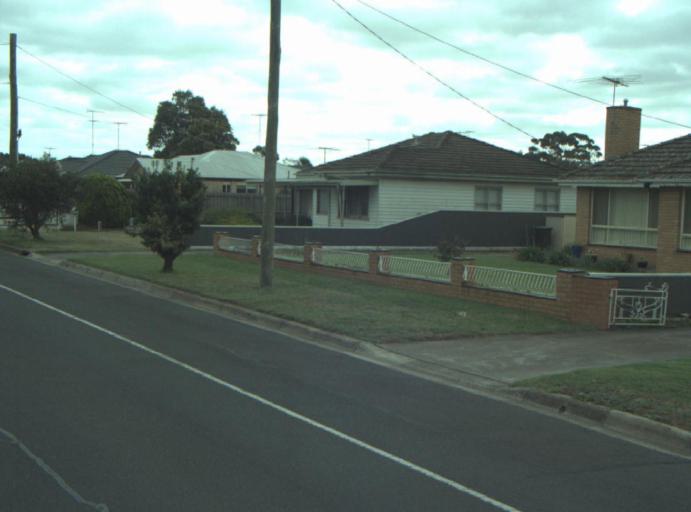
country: AU
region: Victoria
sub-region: Greater Geelong
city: Lara
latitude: -38.0311
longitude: 144.4128
